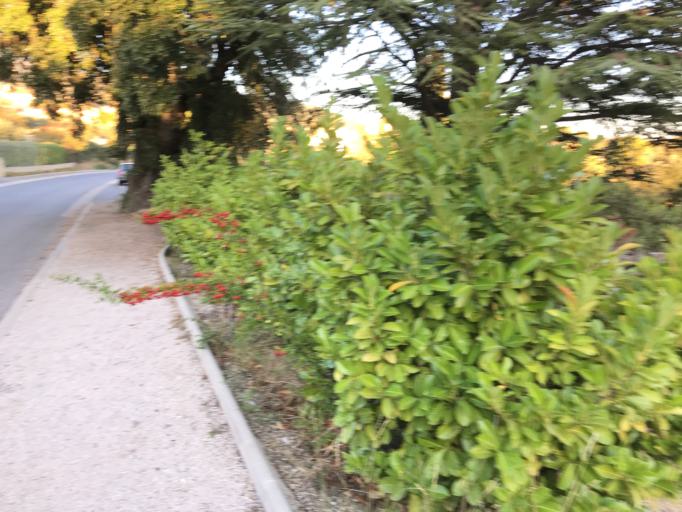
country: FR
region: Provence-Alpes-Cote d'Azur
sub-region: Departement du Vaucluse
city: Ansouis
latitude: 43.7843
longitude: 5.4947
